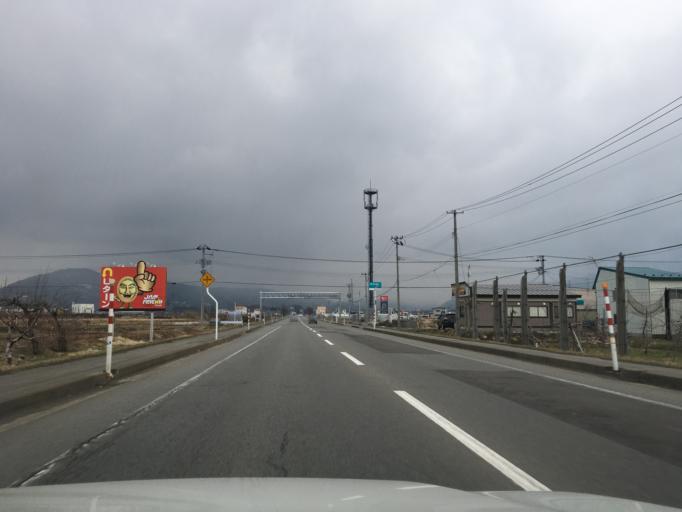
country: JP
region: Aomori
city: Kuroishi
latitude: 40.5805
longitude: 140.5686
